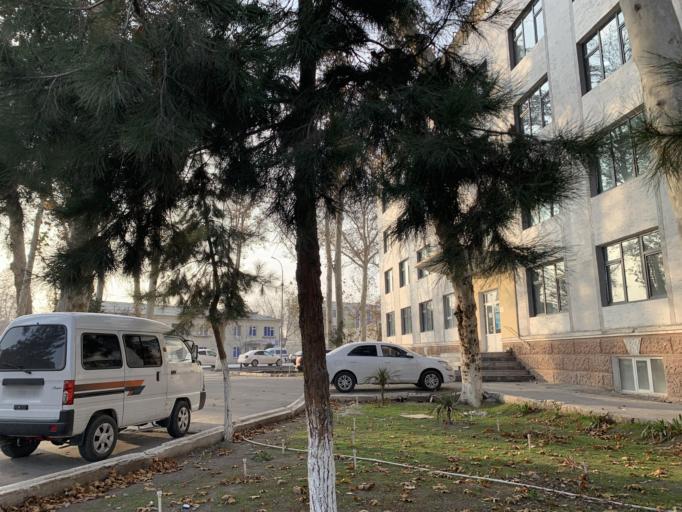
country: UZ
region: Fergana
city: Qo`qon
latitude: 40.5410
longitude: 70.9231
